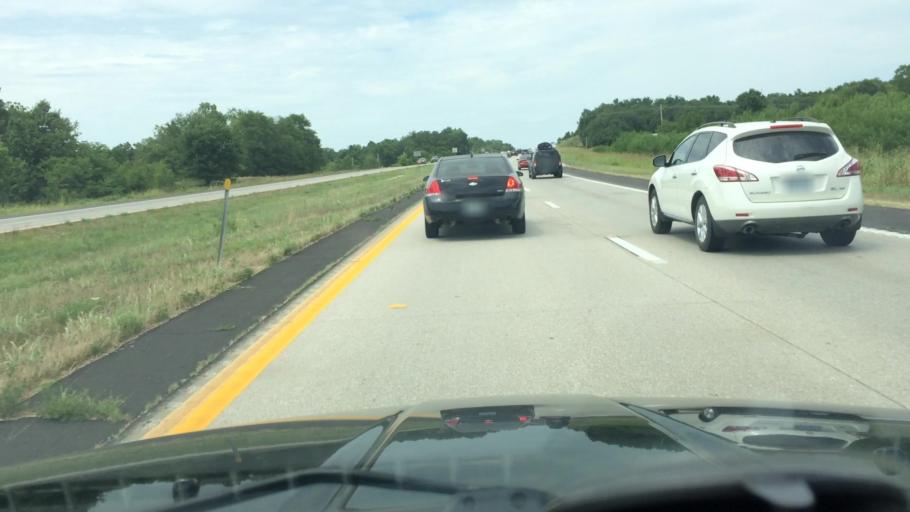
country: US
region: Missouri
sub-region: Greene County
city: Willard
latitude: 37.4342
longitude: -93.3555
